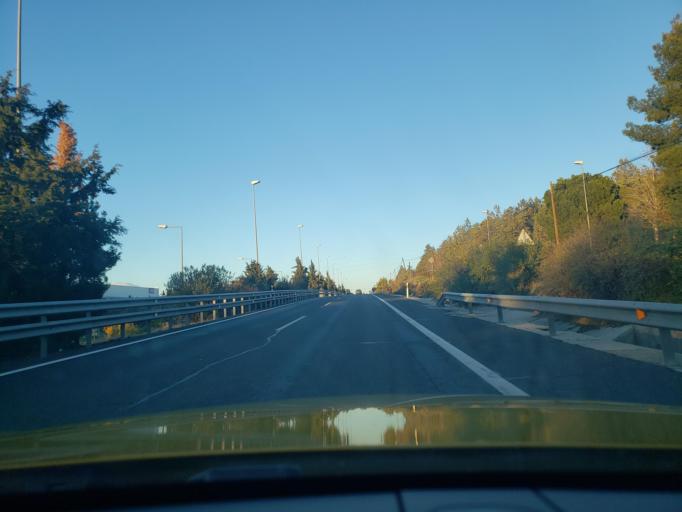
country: ES
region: Castille-La Mancha
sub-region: Province of Toledo
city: Bargas
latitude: 39.9017
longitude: -4.0145
